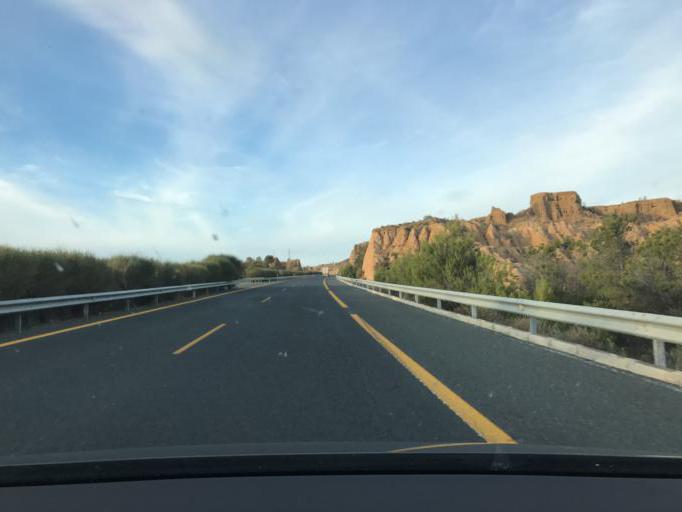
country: ES
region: Andalusia
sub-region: Provincia de Granada
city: Guadix
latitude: 37.3090
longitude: -3.1122
